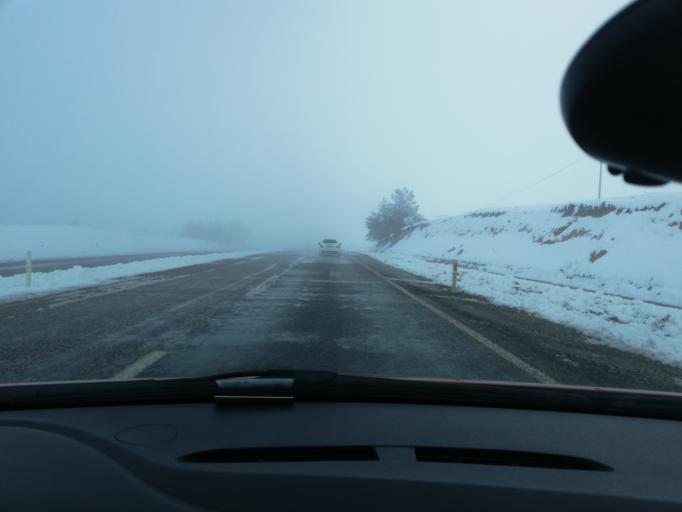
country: TR
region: Kastamonu
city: Akkaya
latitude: 41.2983
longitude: 33.5180
